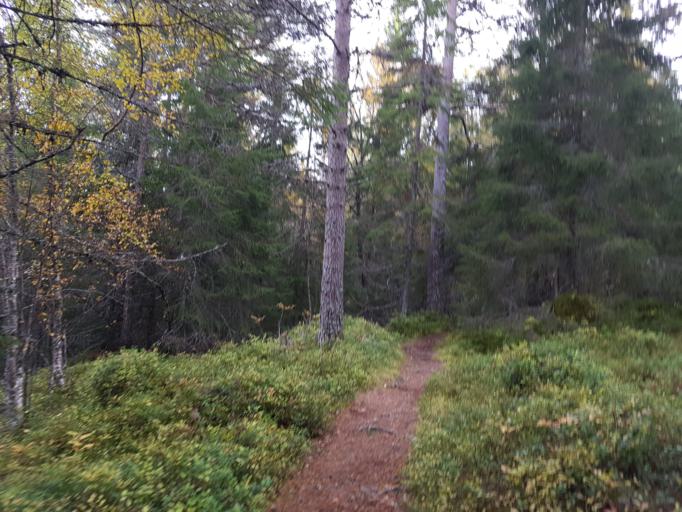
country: NO
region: Sor-Trondelag
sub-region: Trondheim
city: Trondheim
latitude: 63.4437
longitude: 10.3096
